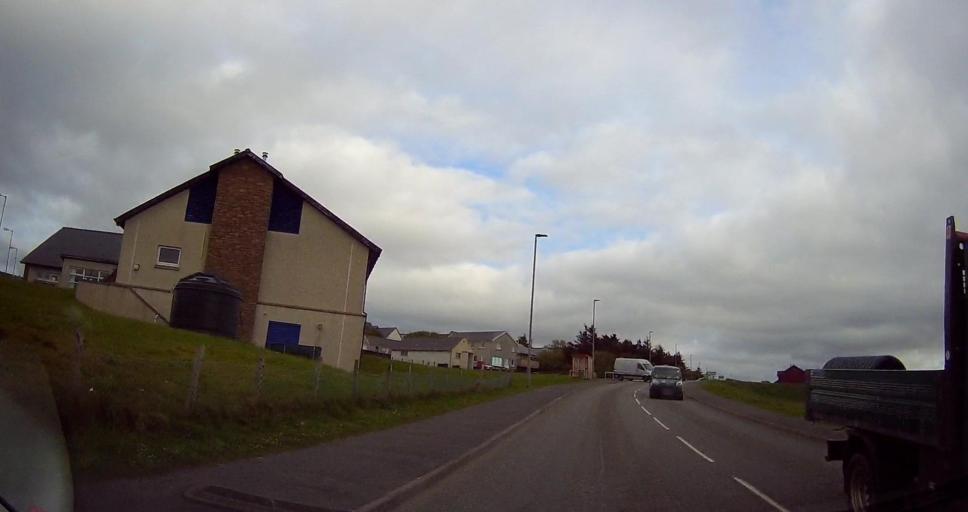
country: GB
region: Scotland
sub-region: Shetland Islands
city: Lerwick
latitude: 60.3945
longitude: -1.3516
